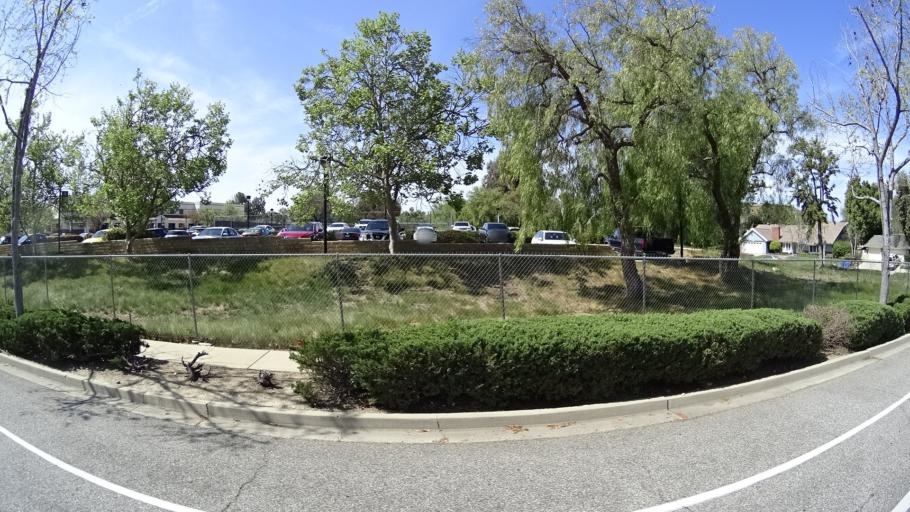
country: US
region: California
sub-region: Ventura County
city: Thousand Oaks
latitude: 34.2048
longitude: -118.8772
